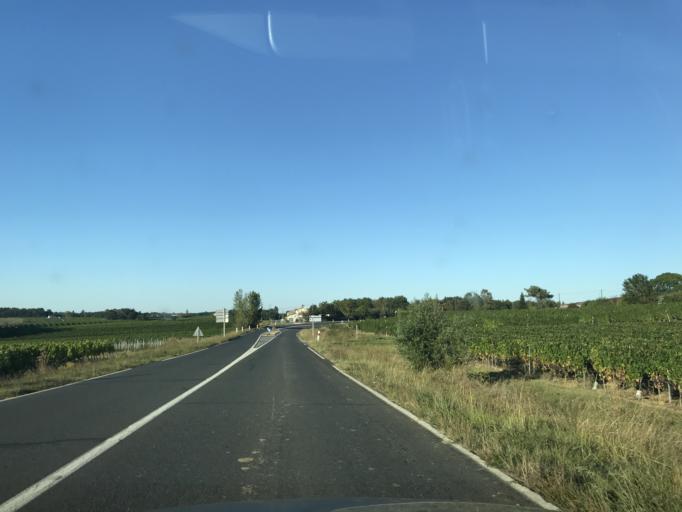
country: FR
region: Aquitaine
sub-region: Departement de la Gironde
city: Sauveterre-de-Guyenne
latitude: 44.6484
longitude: -0.1238
